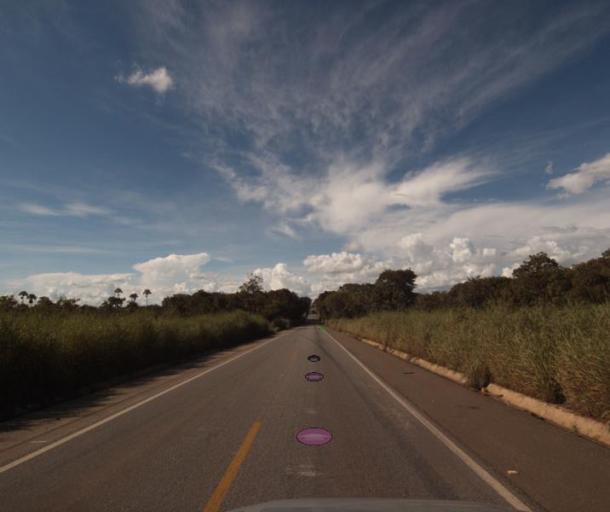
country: BR
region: Goias
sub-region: Porangatu
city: Porangatu
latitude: -13.0330
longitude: -49.1701
